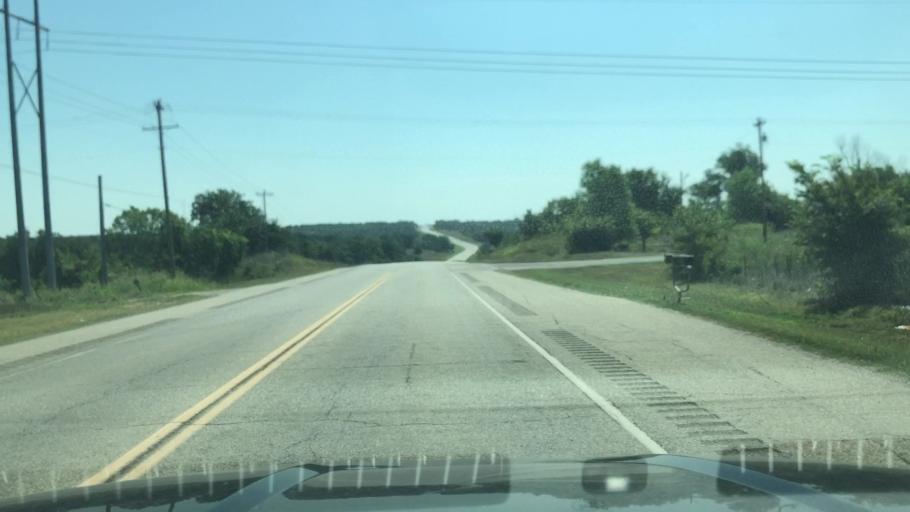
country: US
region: Oklahoma
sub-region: Creek County
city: Mannford
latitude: 36.0031
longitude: -96.4057
